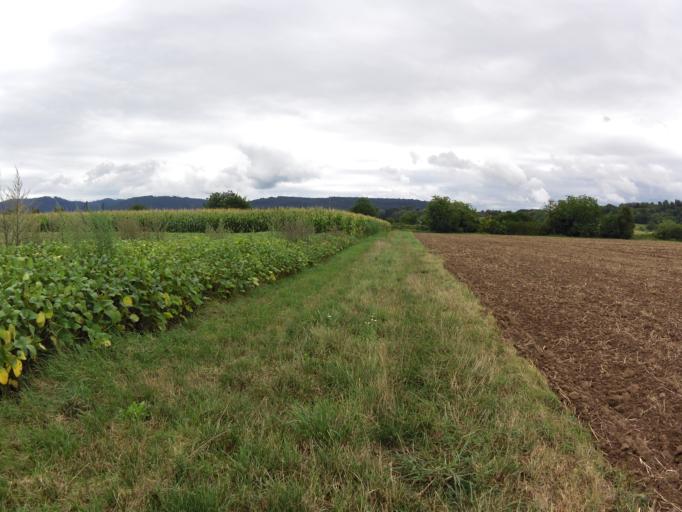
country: DE
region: Baden-Wuerttemberg
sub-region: Freiburg Region
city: Lahr
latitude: 48.3643
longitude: 7.8490
